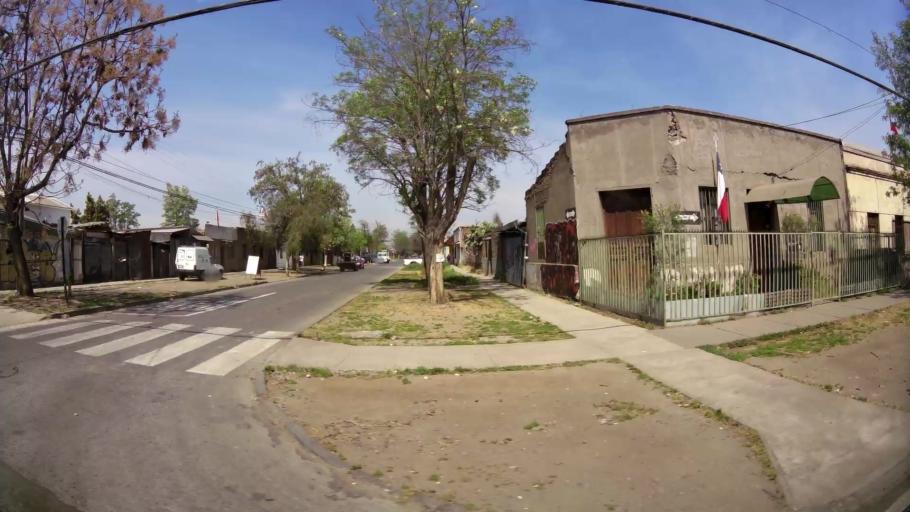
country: CL
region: Santiago Metropolitan
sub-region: Provincia de Santiago
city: Lo Prado
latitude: -33.4270
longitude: -70.7125
